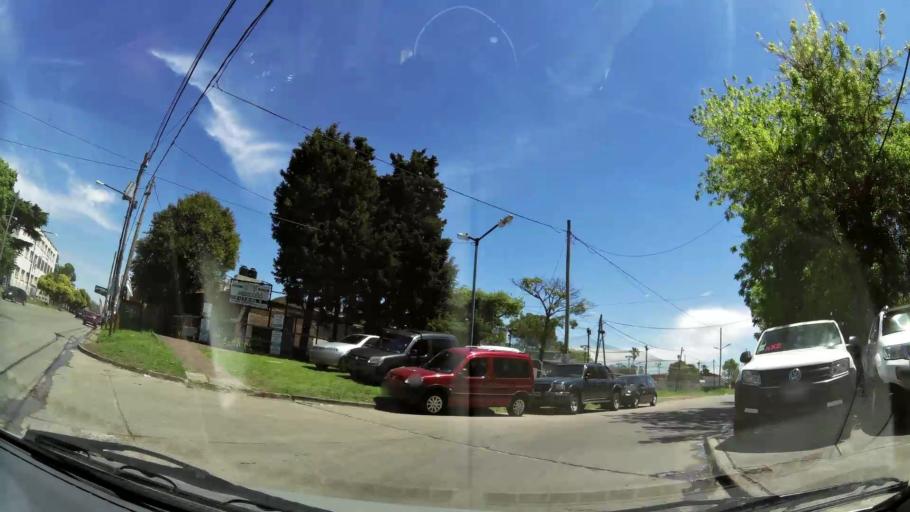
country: AR
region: Buenos Aires
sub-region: Partido de Quilmes
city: Quilmes
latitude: -34.7374
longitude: -58.2798
